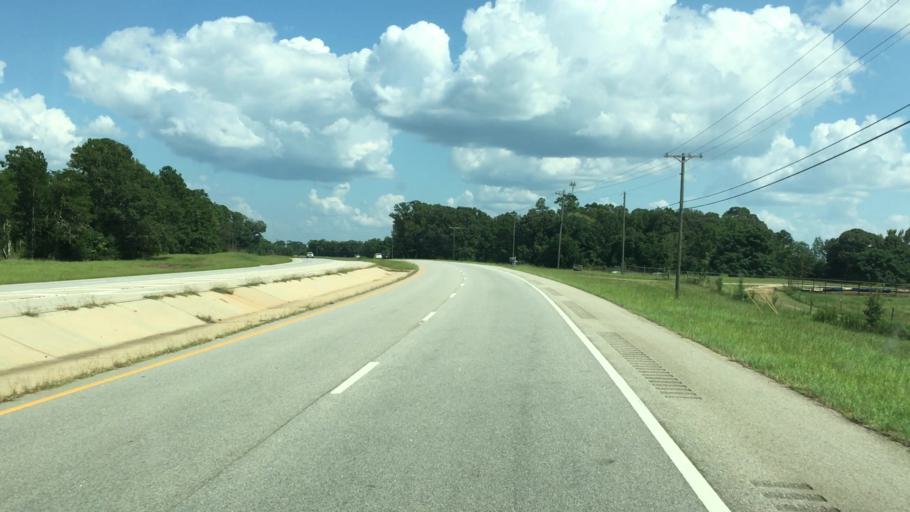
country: US
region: Georgia
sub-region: Putnam County
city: Eatonton
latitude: 33.2706
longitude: -83.3441
